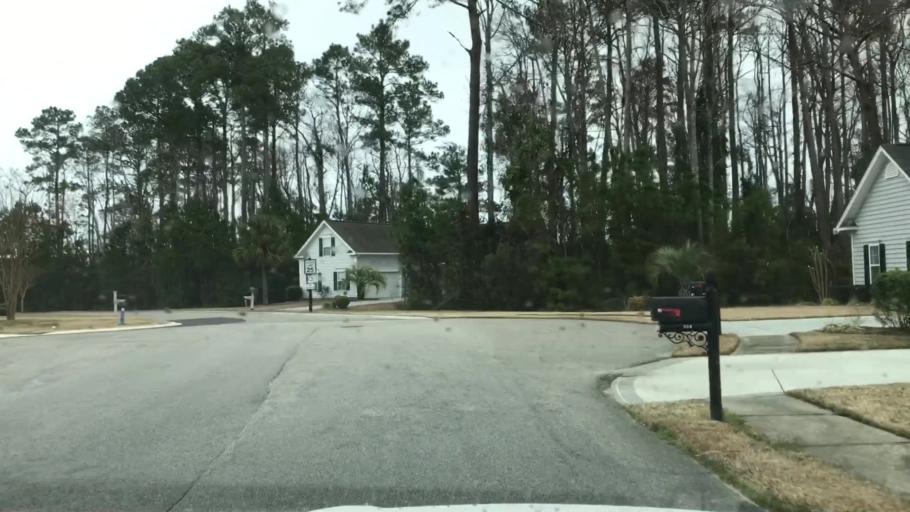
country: US
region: South Carolina
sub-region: Horry County
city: Red Hill
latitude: 33.7758
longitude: -79.0077
